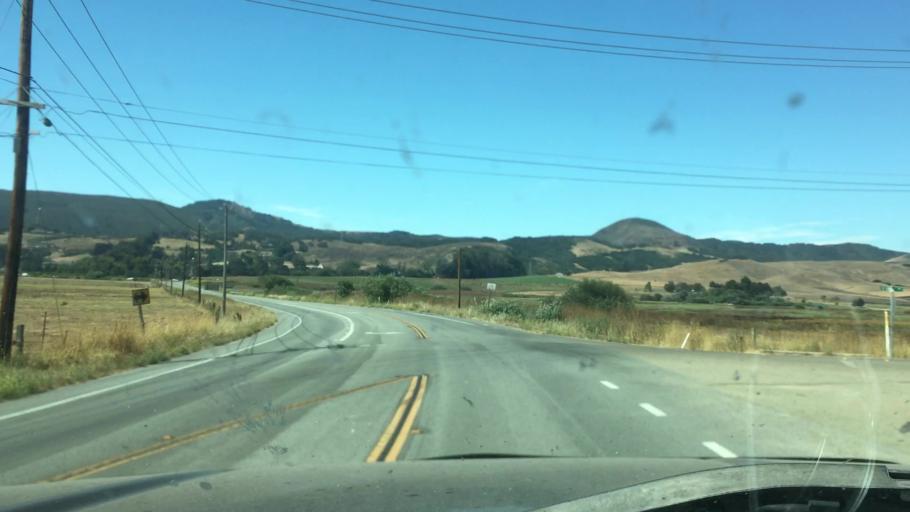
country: US
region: California
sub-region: San Luis Obispo County
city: San Luis Obispo
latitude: 35.2818
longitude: -120.7083
